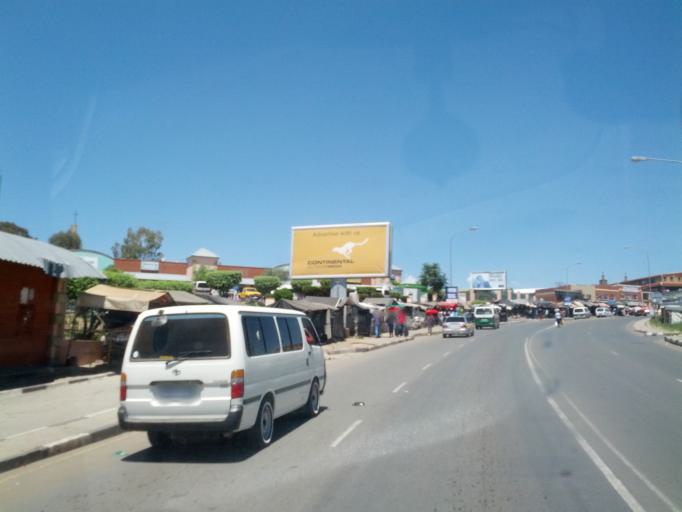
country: LS
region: Maseru
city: Maseru
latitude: -29.3139
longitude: 27.4928
